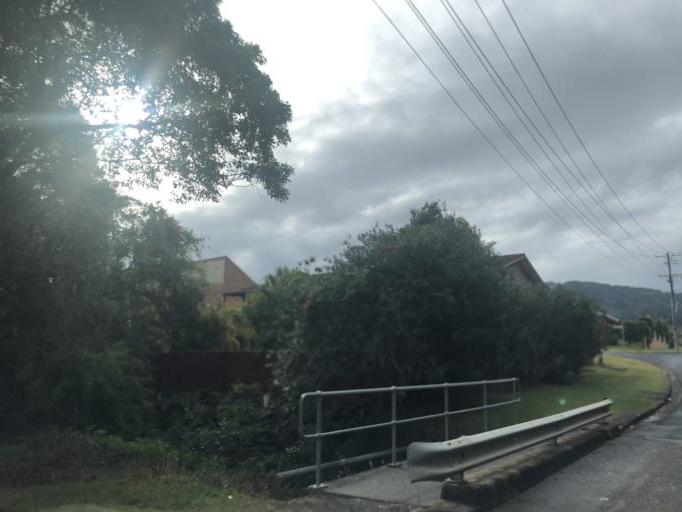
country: AU
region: New South Wales
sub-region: Coffs Harbour
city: Coffs Harbour
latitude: -30.2862
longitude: 153.1110
